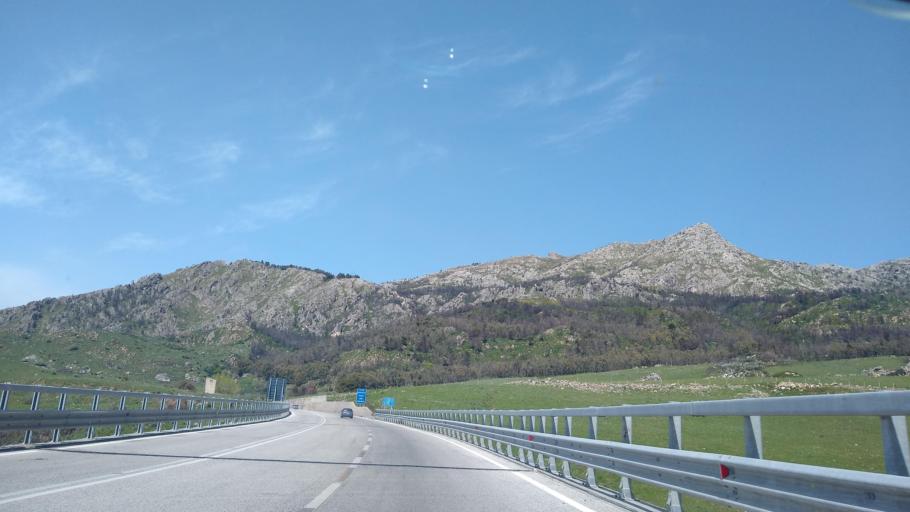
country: IT
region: Sicily
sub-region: Palermo
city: Piana degli Albanesi
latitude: 37.9833
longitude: 13.2374
